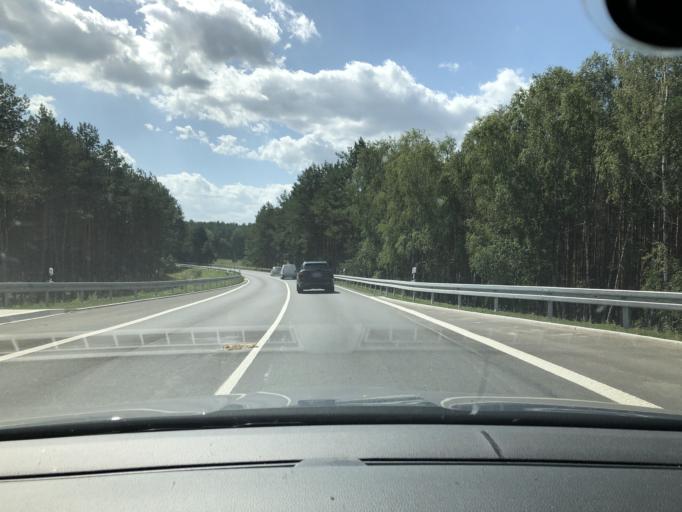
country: DE
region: Brandenburg
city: Wittstock
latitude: 53.1034
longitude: 12.4833
